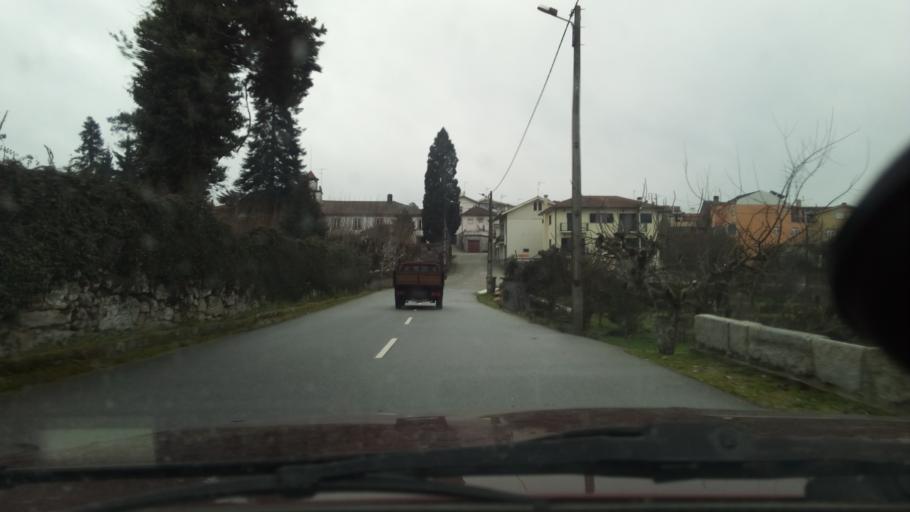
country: PT
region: Viseu
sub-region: Mangualde
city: Mangualde
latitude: 40.6086
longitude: -7.8155
